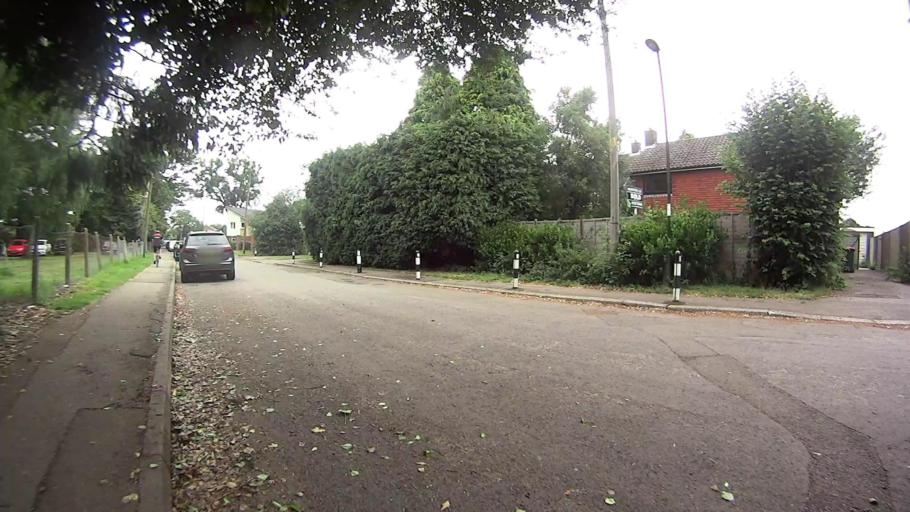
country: GB
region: England
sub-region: West Sussex
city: Langley Green
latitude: 51.1207
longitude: -0.2049
